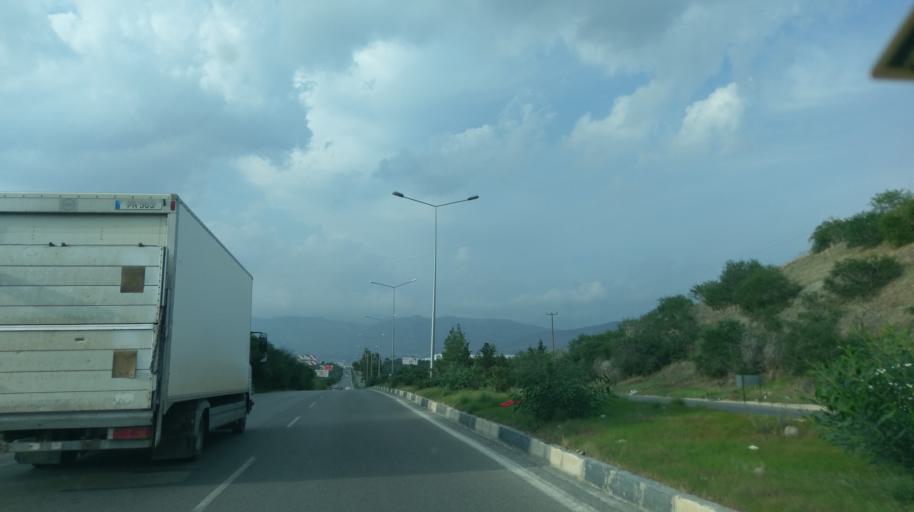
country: CY
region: Lefkosia
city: Nicosia
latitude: 35.2426
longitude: 33.3092
